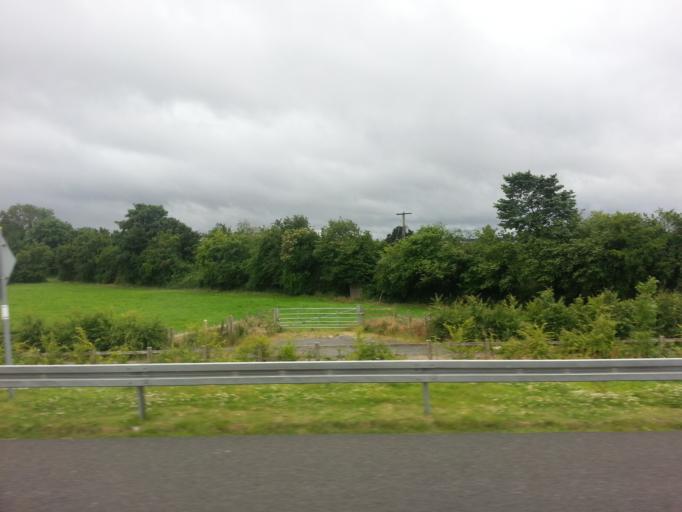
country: IE
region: Leinster
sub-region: Kilkenny
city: Kilkenny
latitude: 52.6591
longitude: -7.2180
